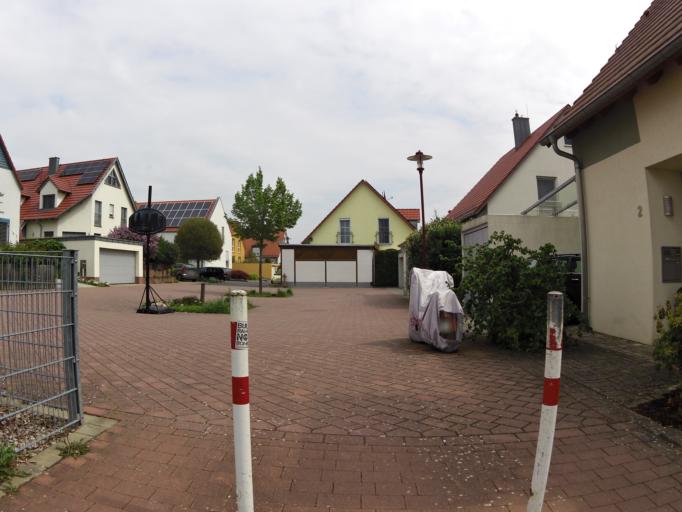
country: DE
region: Bavaria
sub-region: Regierungsbezirk Unterfranken
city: Kurnach
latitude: 49.8510
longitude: 10.0479
